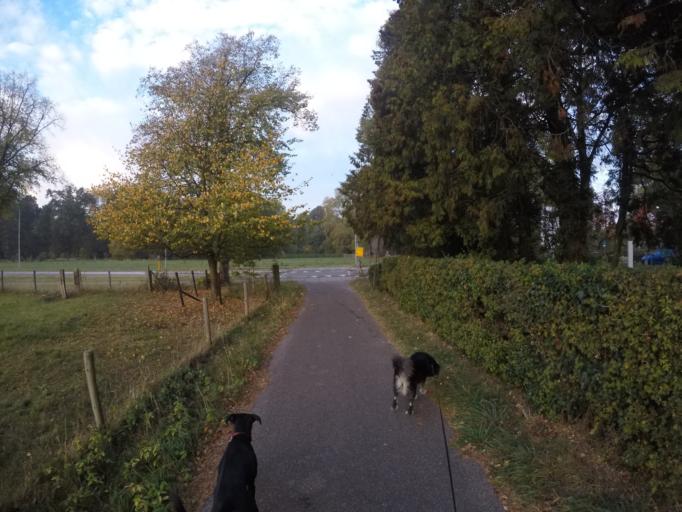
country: NL
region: Gelderland
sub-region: Gemeente Zevenaar
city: Zevenaar
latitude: 51.9269
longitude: 6.0807
